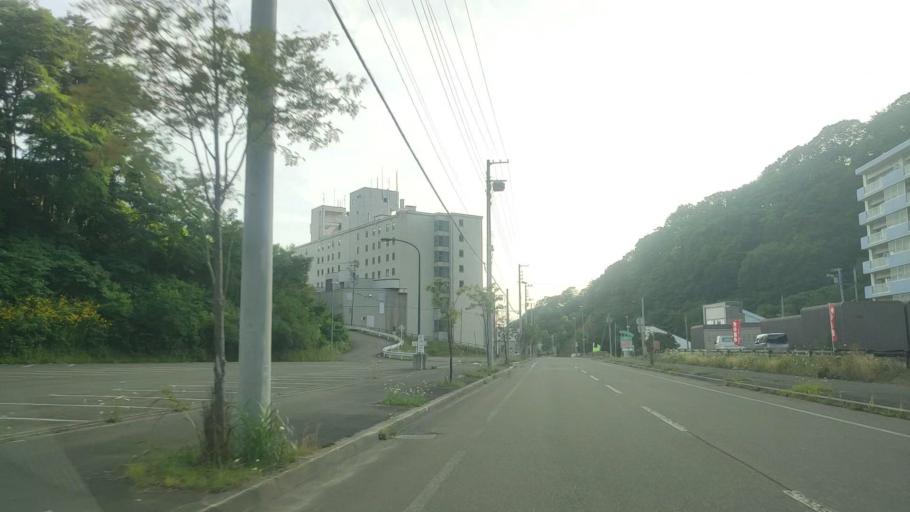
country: JP
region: Hokkaido
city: Iwamizawa
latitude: 43.0606
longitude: 141.9781
